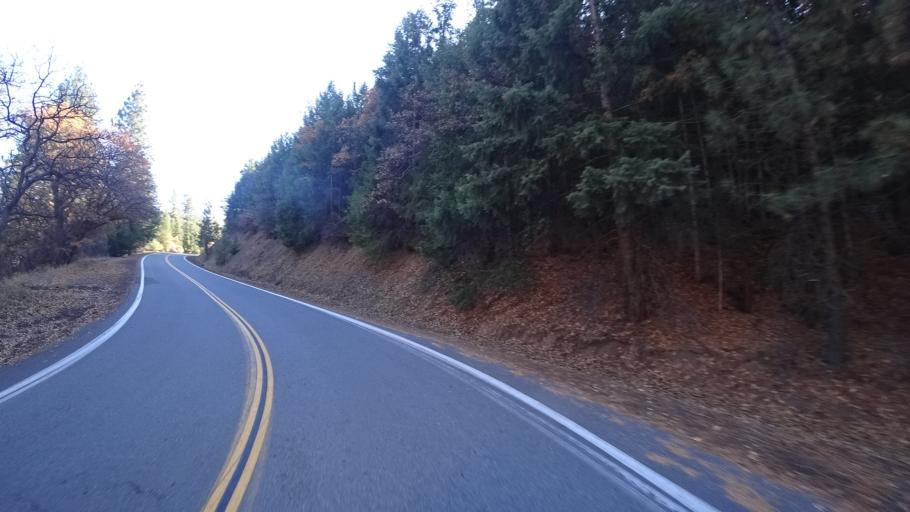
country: US
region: California
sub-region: Siskiyou County
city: Weed
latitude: 41.4561
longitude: -122.6387
